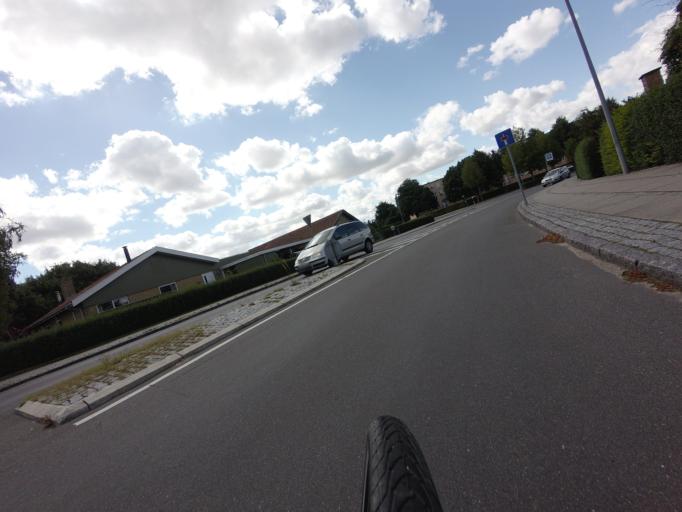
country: DK
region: Central Jutland
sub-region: Horsens Kommune
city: Horsens
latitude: 55.8724
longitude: 9.8280
